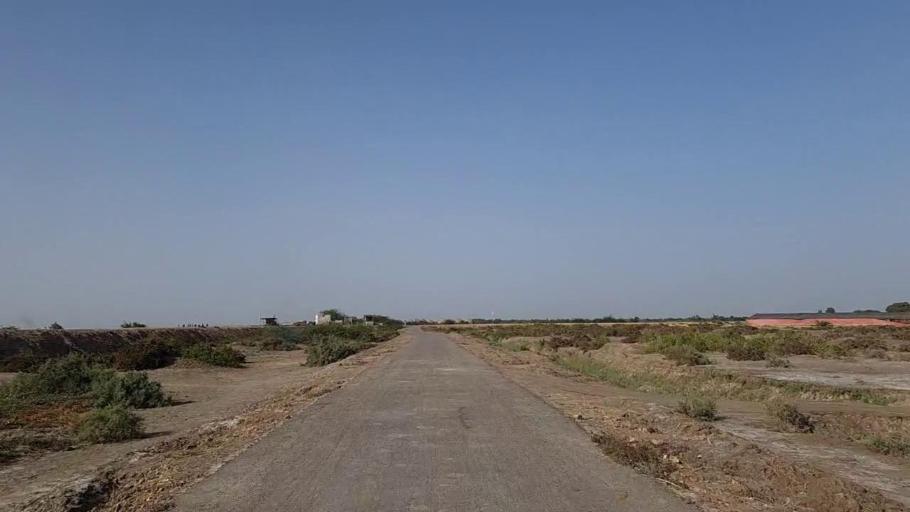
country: PK
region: Sindh
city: Jati
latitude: 24.3063
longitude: 68.1961
